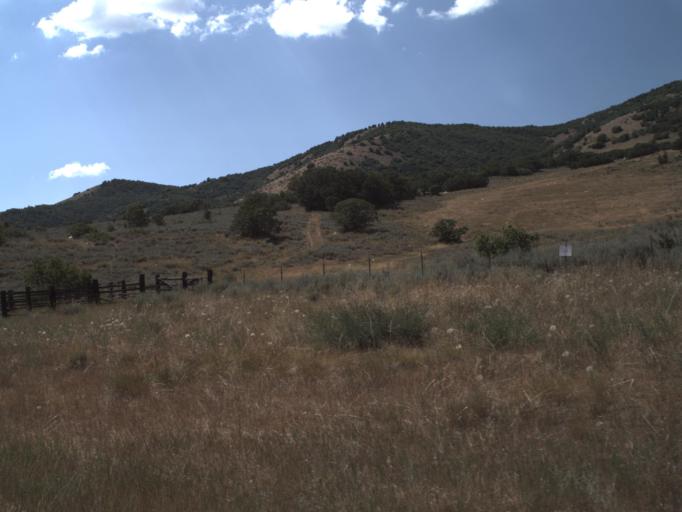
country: US
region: Utah
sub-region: Weber County
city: Wolf Creek
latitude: 41.2643
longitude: -111.6932
